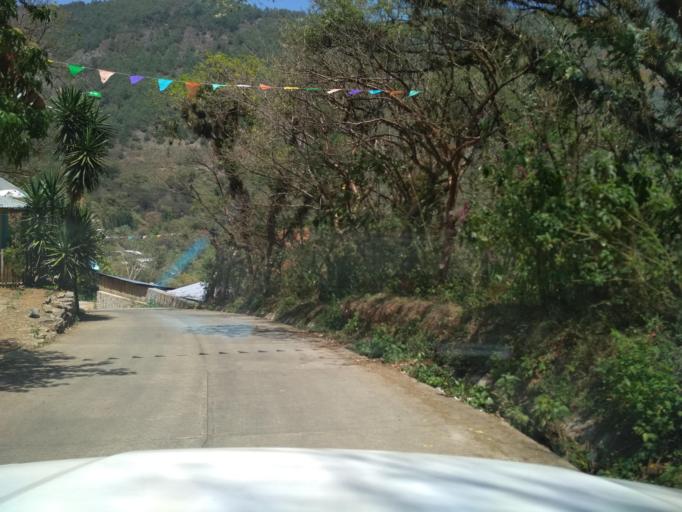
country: MX
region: Veracruz
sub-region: Tlilapan
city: Tonalixco
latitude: 18.7804
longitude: -97.0799
